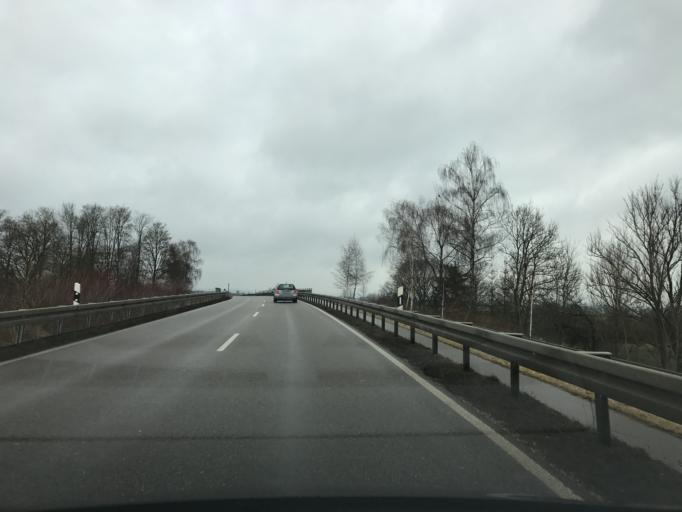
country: DE
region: Baden-Wuerttemberg
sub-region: Tuebingen Region
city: Laupheim
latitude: 48.2486
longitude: 9.8578
